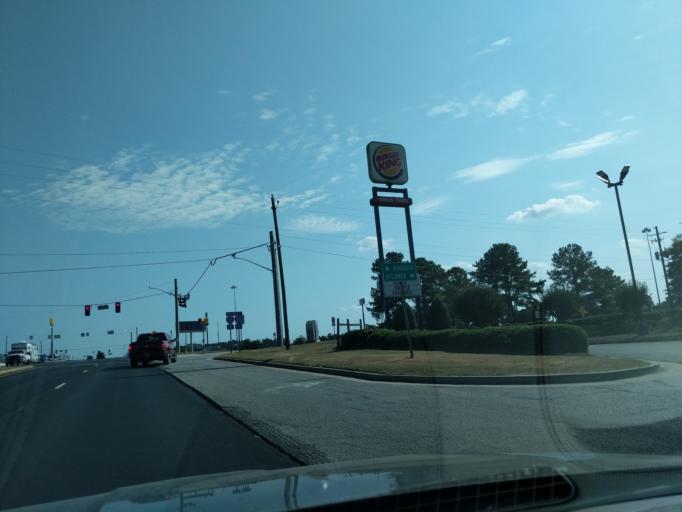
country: US
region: Georgia
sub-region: Columbia County
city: Evans
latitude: 33.4839
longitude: -82.1322
